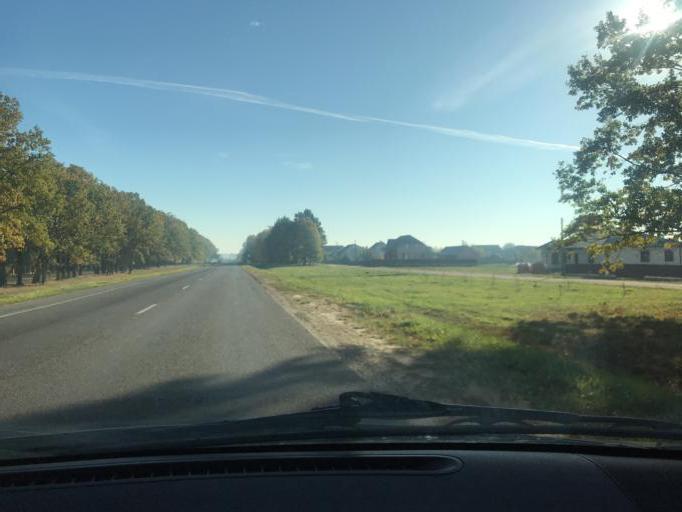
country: BY
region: Brest
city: Ivanava
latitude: 52.1438
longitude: 25.5079
